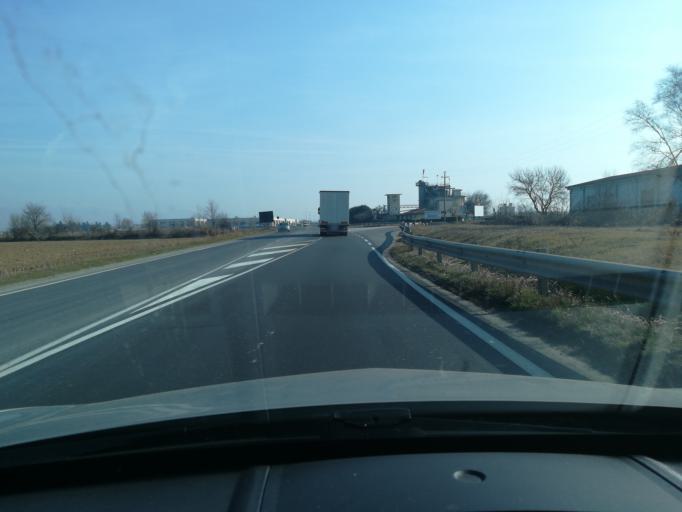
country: IT
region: Lombardy
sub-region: Provincia di Bergamo
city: Palosco
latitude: 45.5985
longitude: 9.8345
